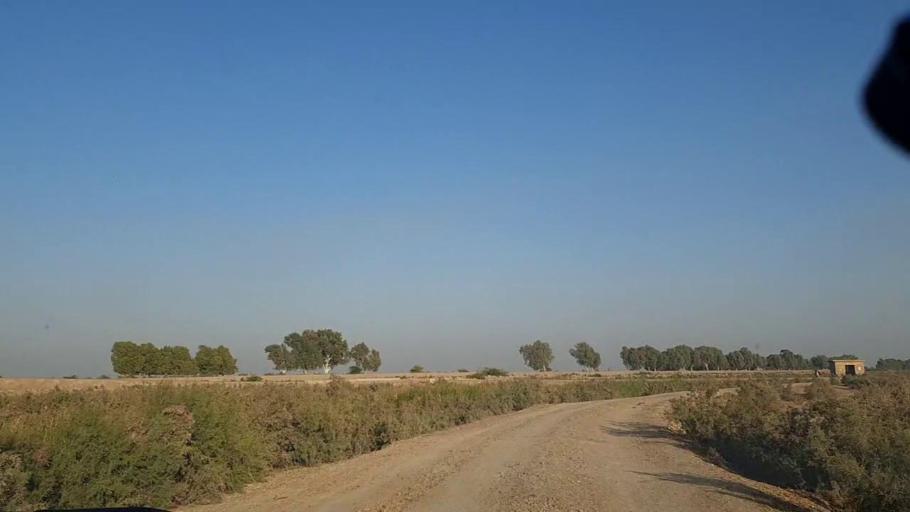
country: PK
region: Sindh
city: Berani
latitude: 25.7005
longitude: 68.9321
